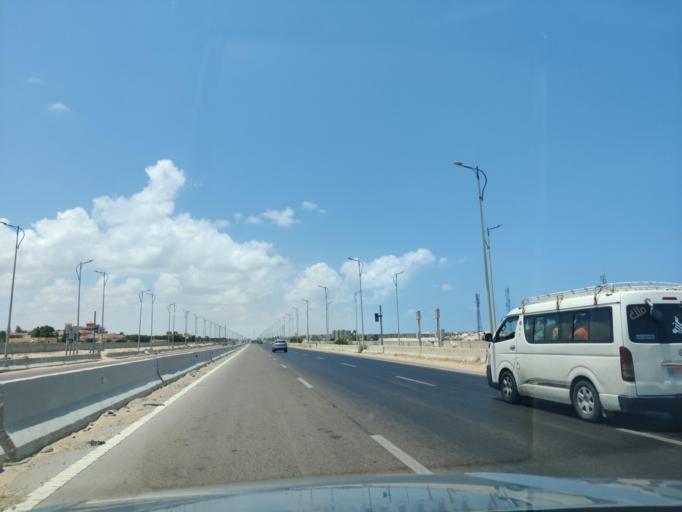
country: EG
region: Muhafazat Matruh
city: Al `Alamayn
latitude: 30.9191
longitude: 29.4530
